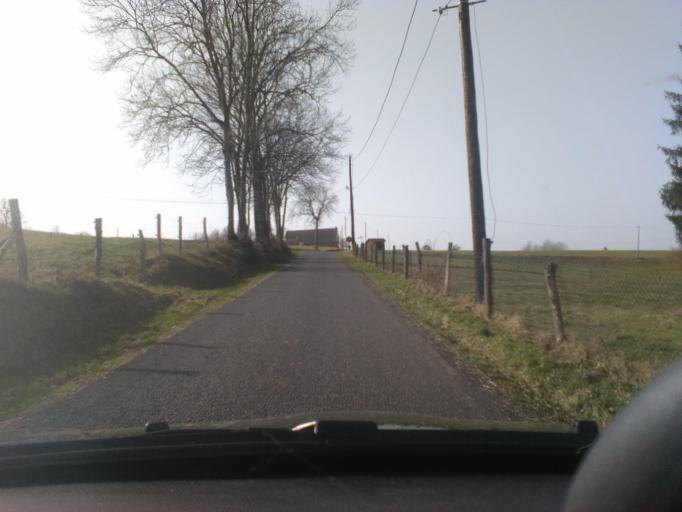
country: FR
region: Lorraine
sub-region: Departement des Vosges
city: Senones
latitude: 48.3525
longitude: 6.9975
